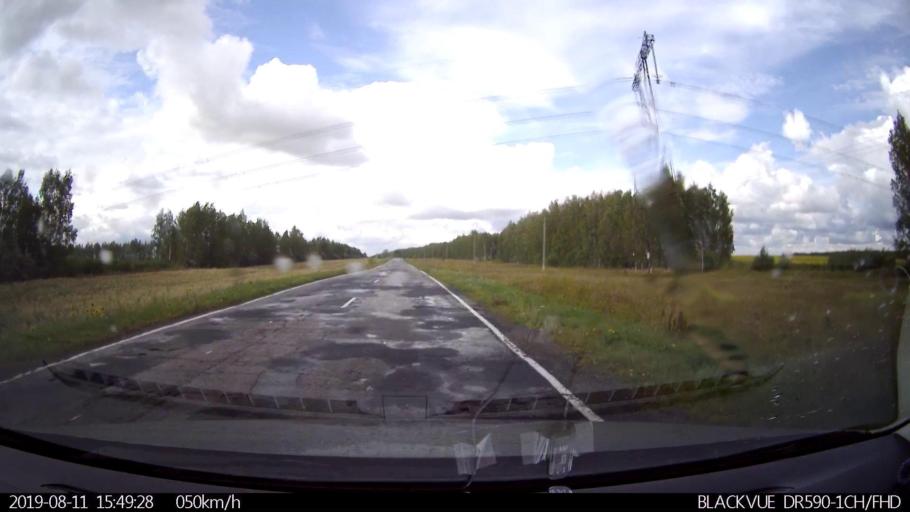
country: RU
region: Ulyanovsk
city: Ignatovka
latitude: 53.9045
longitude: 47.6550
